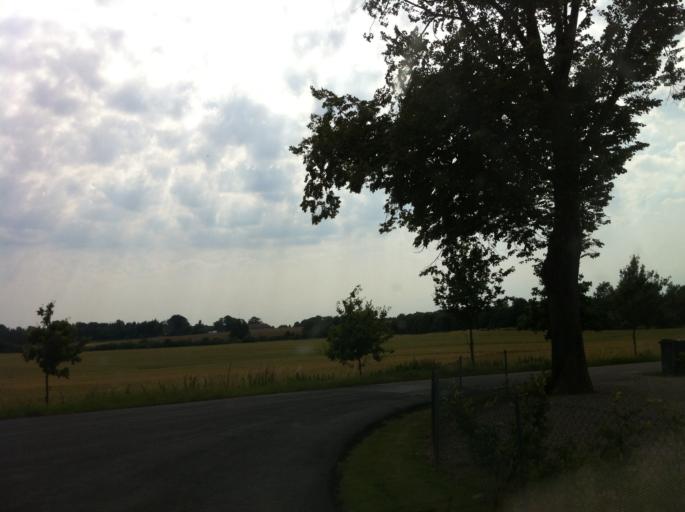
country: SE
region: Skane
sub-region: Eslovs Kommun
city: Eslov
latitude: 55.9182
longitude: 13.2465
